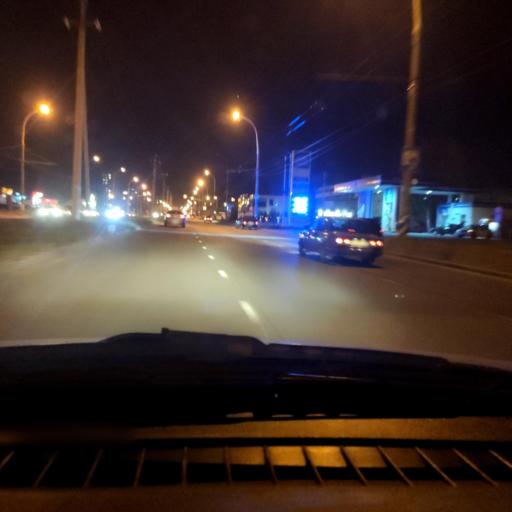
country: RU
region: Samara
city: Tol'yatti
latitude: 53.5409
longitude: 49.3002
